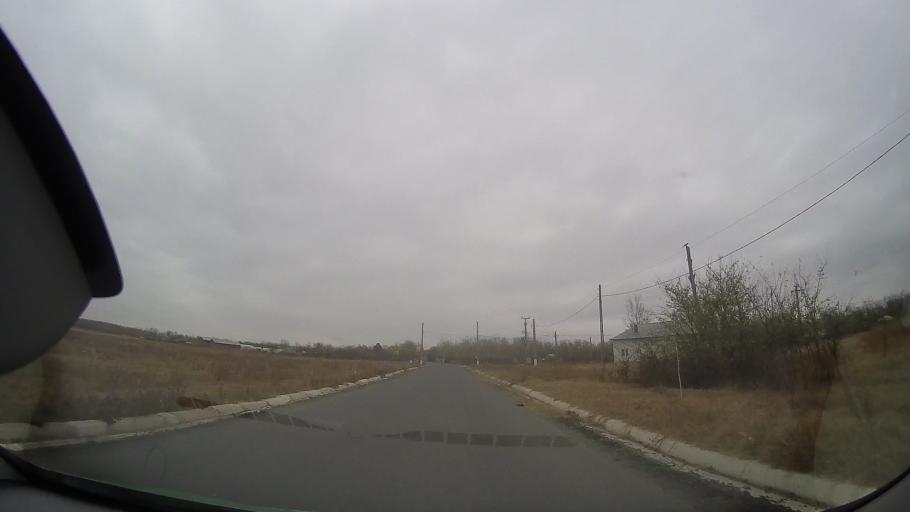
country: RO
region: Braila
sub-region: Comuna Ciocile
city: Ciocile
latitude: 44.8023
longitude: 27.2724
